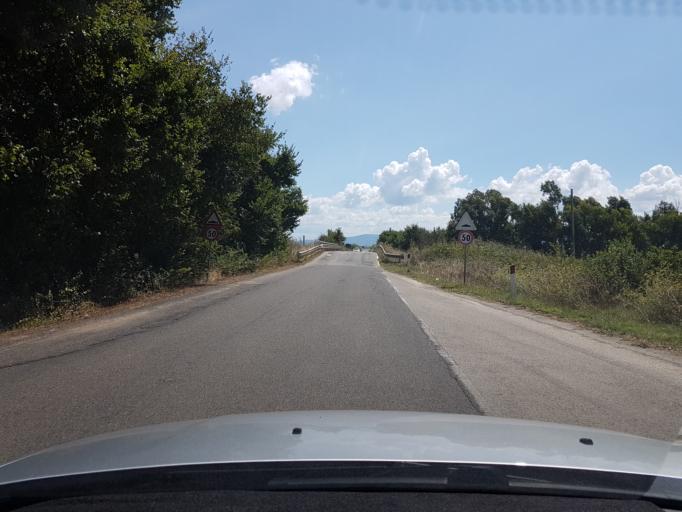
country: IT
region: Sardinia
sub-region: Provincia di Oristano
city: Solanas
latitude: 39.9205
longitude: 8.5476
